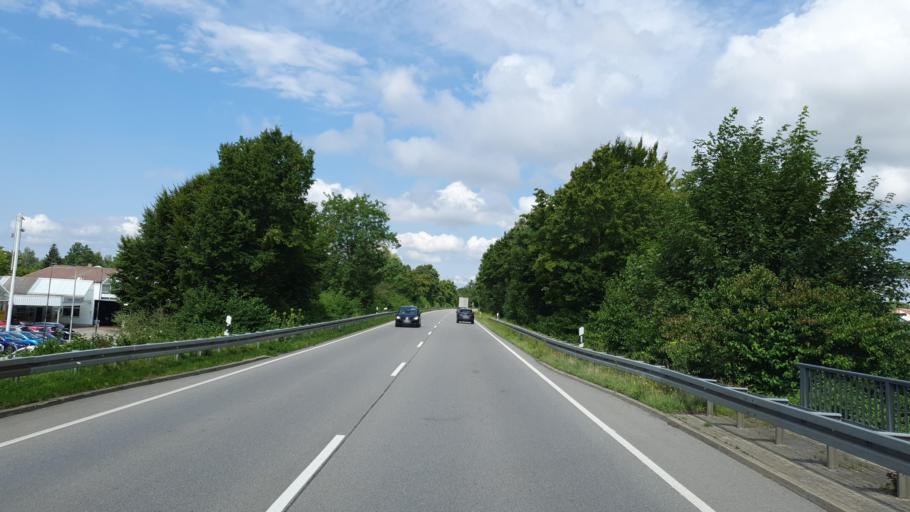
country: DE
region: Baden-Wuerttemberg
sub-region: Tuebingen Region
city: Friedrichshafen
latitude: 47.6514
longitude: 9.5056
